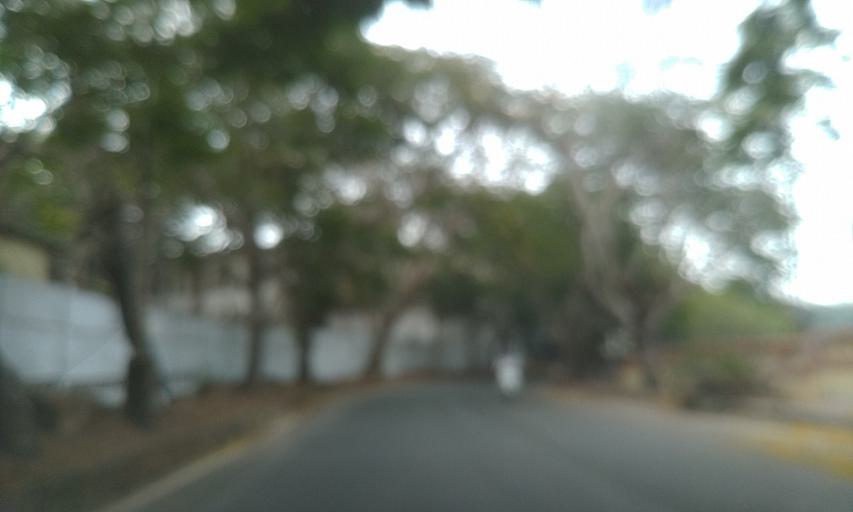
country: IN
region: Goa
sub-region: North Goa
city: Panaji
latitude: 15.4893
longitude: 73.8256
